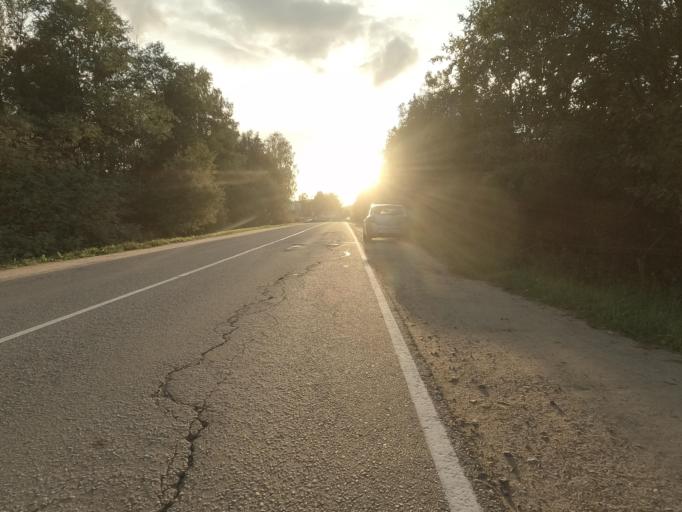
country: RU
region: Leningrad
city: Mga
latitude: 59.7627
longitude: 30.9893
